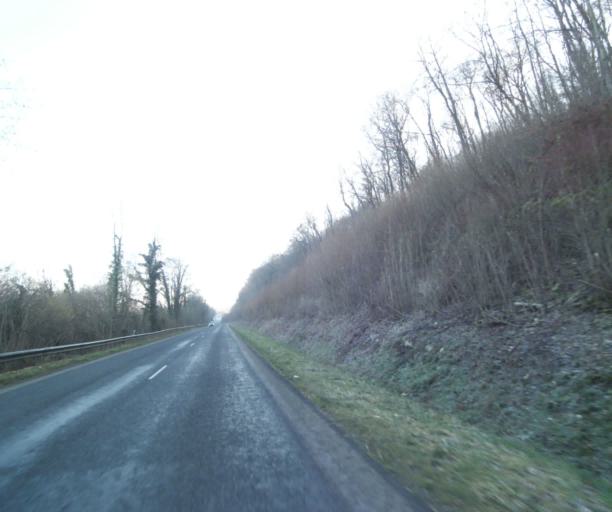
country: FR
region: Champagne-Ardenne
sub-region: Departement de la Haute-Marne
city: Bienville
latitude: 48.5550
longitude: 5.0662
